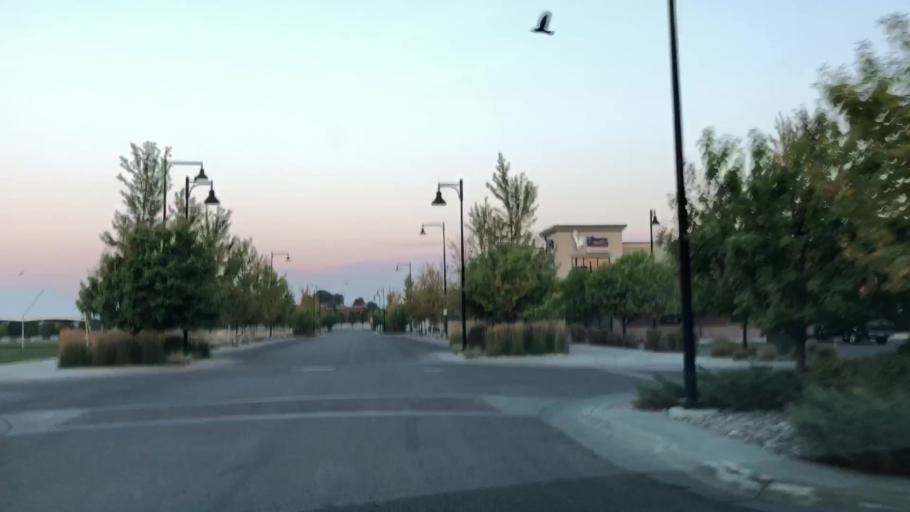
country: US
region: Idaho
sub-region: Bonneville County
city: Idaho Falls
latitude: 43.4842
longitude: -112.0518
